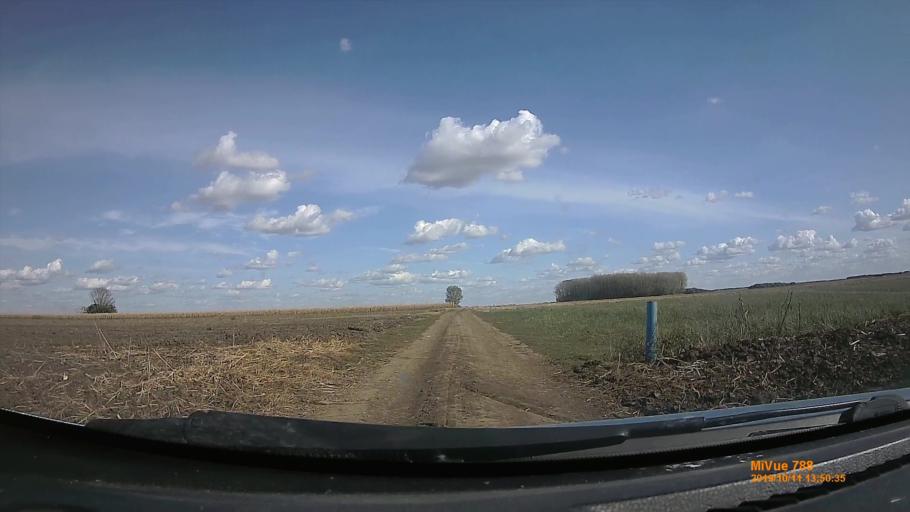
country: HU
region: Hajdu-Bihar
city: Hajduszoboszlo
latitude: 47.5402
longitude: 21.3982
